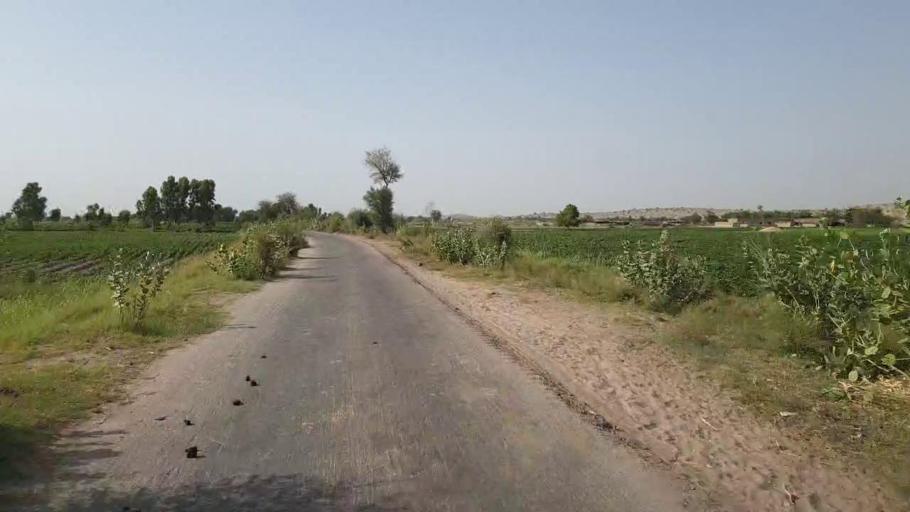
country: PK
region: Sindh
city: Kandiari
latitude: 26.6950
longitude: 68.9647
